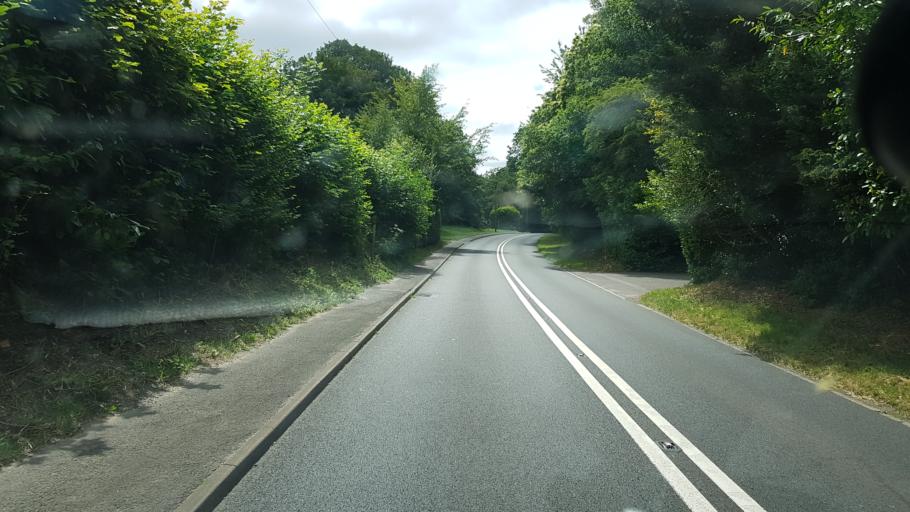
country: GB
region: England
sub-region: Surrey
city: Felbridge
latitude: 51.1468
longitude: -0.0421
